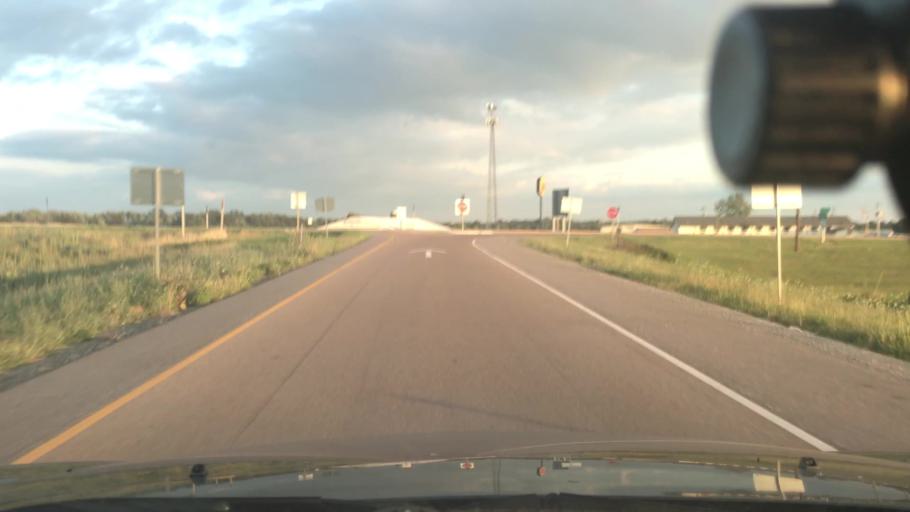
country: US
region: Illinois
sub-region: Washington County
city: Okawville
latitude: 38.4392
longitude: -89.5330
